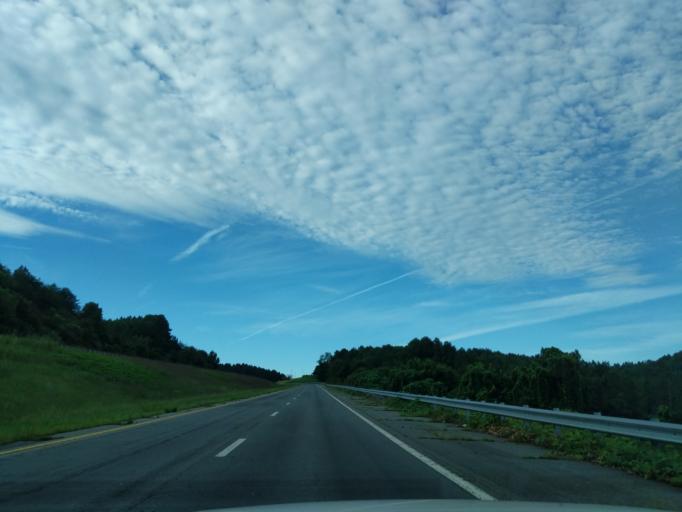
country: US
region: Georgia
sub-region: Fannin County
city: McCaysville
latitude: 35.0146
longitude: -84.3830
